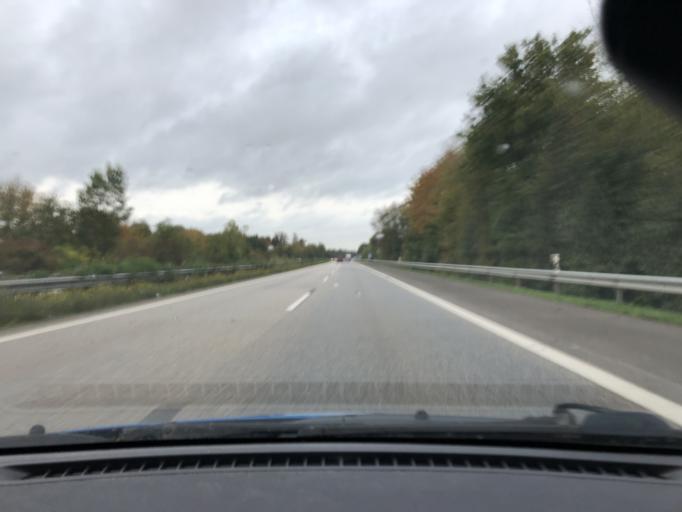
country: DE
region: Schleswig-Holstein
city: Rumohr
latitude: 54.2367
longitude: 10.0200
